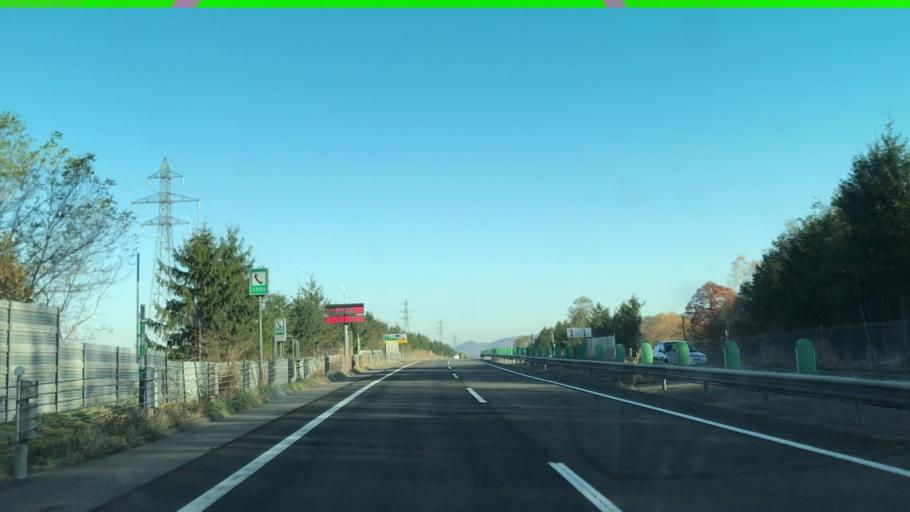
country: JP
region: Hokkaido
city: Sunagawa
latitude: 43.4230
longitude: 141.9114
